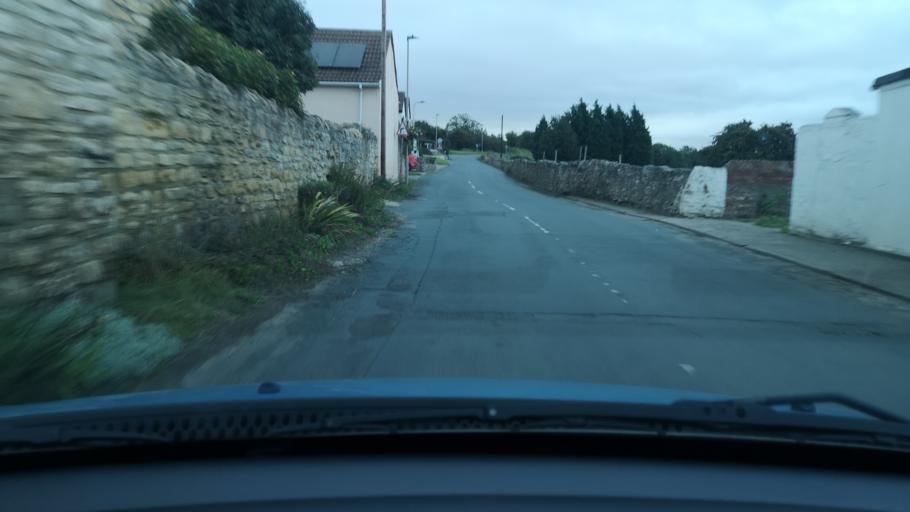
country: GB
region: England
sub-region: Doncaster
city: Norton
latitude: 53.6443
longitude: -1.2054
